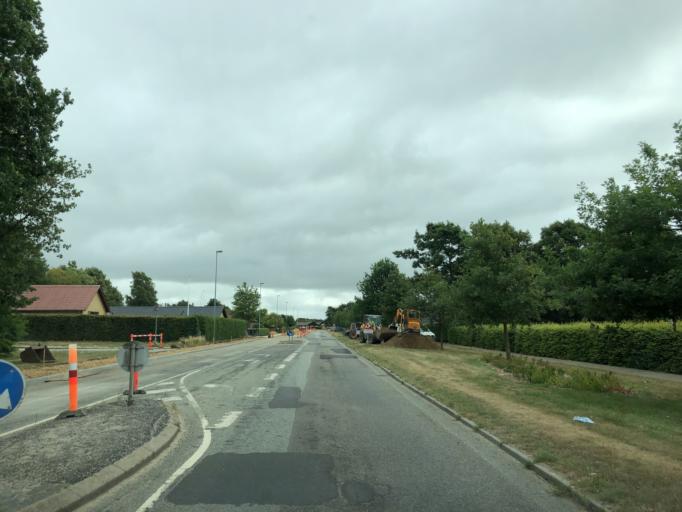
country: DK
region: Central Jutland
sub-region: Herning Kommune
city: Vildbjerg
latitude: 56.1966
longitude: 8.7599
